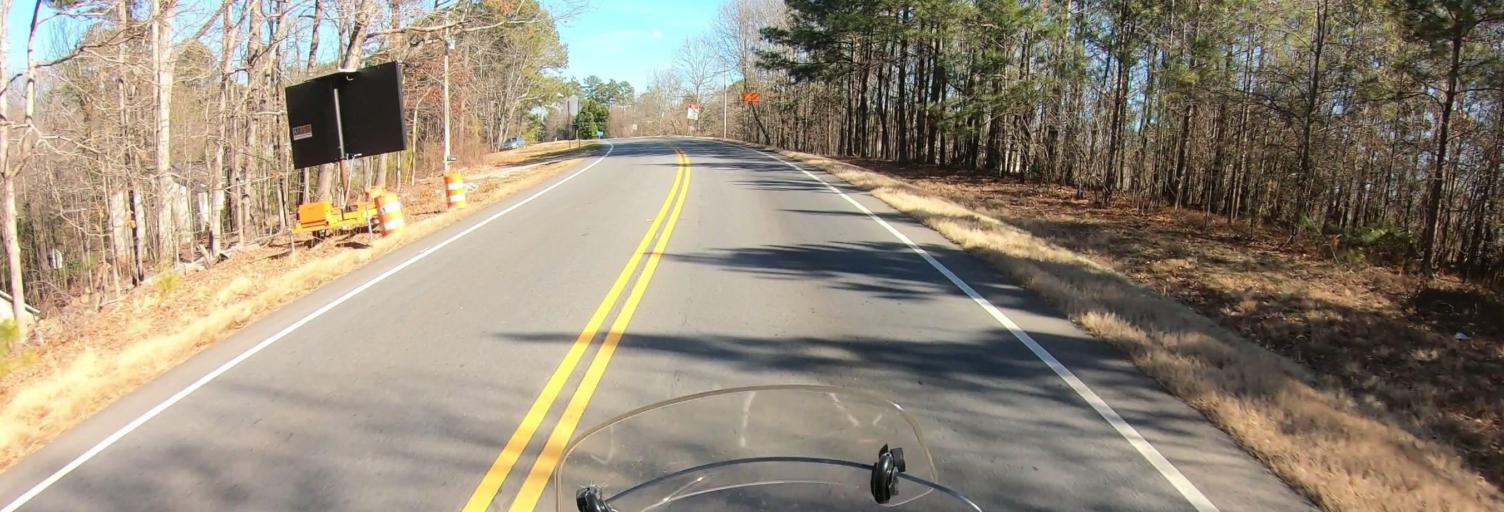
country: US
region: Georgia
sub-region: Hall County
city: Oakwood
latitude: 34.2592
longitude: -83.9432
